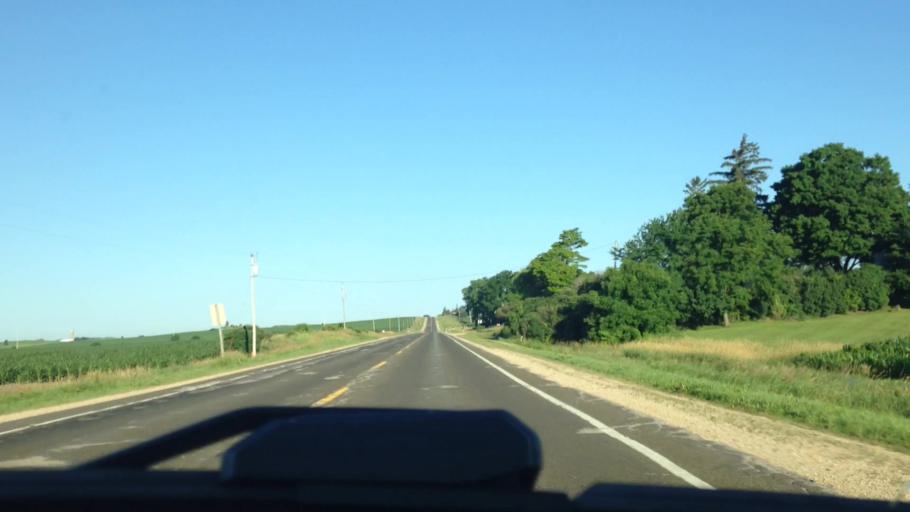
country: US
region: Wisconsin
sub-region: Dane County
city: De Forest
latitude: 43.3323
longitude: -89.3365
